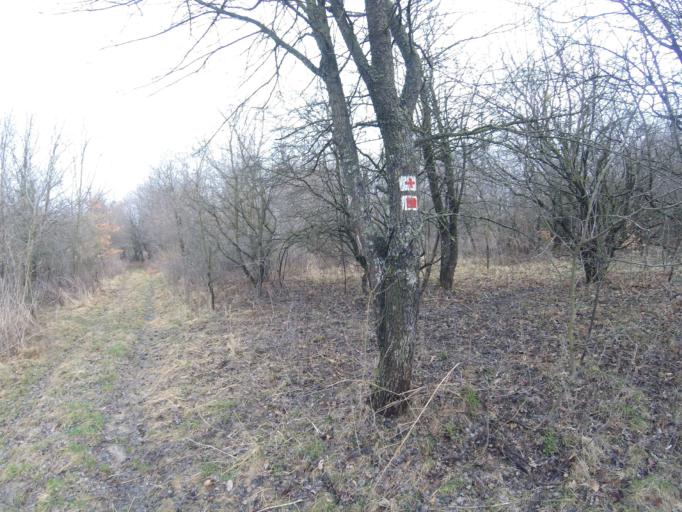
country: HU
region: Veszprem
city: Zirc
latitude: 47.3312
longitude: 17.8661
